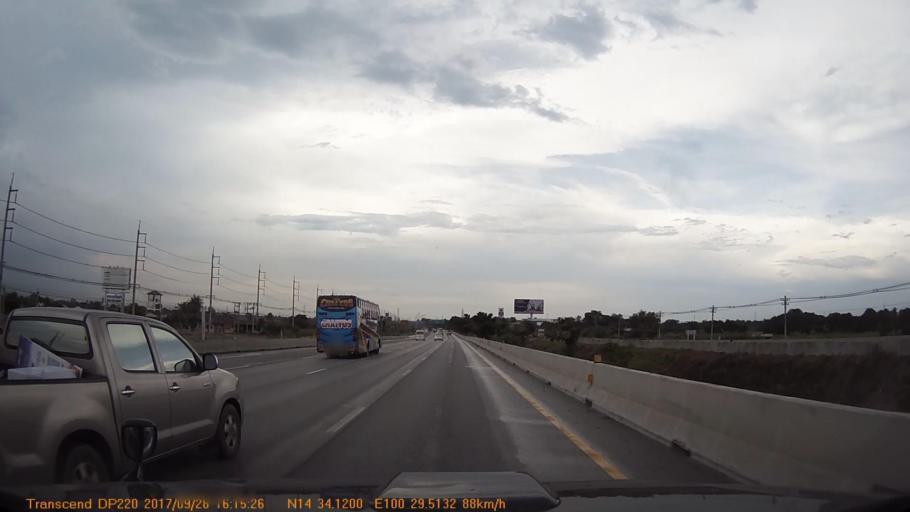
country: TH
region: Ang Thong
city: Ang Thong
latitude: 14.5692
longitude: 100.4916
